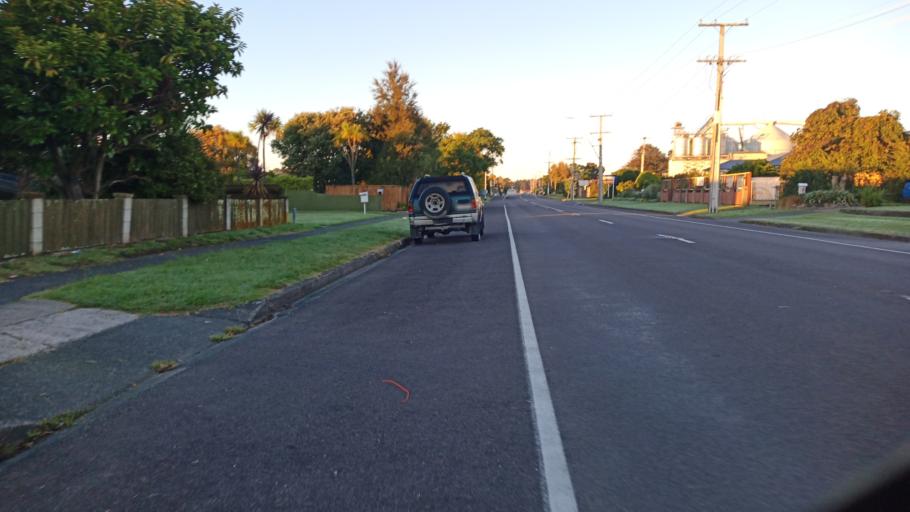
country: NZ
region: Gisborne
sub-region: Gisborne District
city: Gisborne
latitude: -38.6562
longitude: 177.9885
